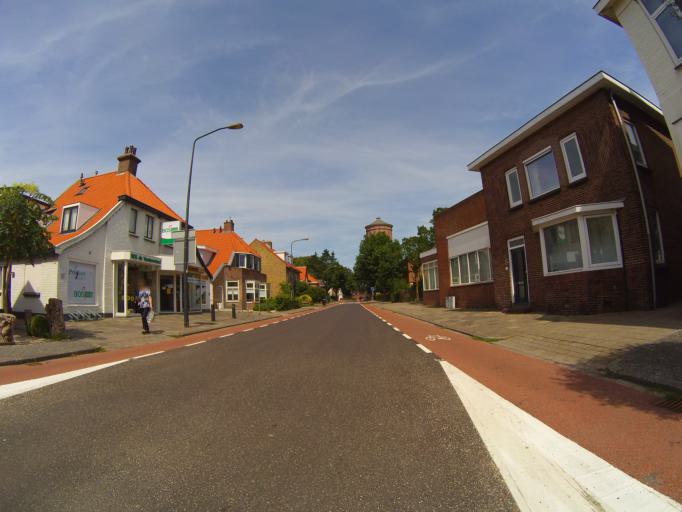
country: NL
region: Utrecht
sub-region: Gemeente Zeist
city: Zeist
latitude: 52.0896
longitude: 5.2419
